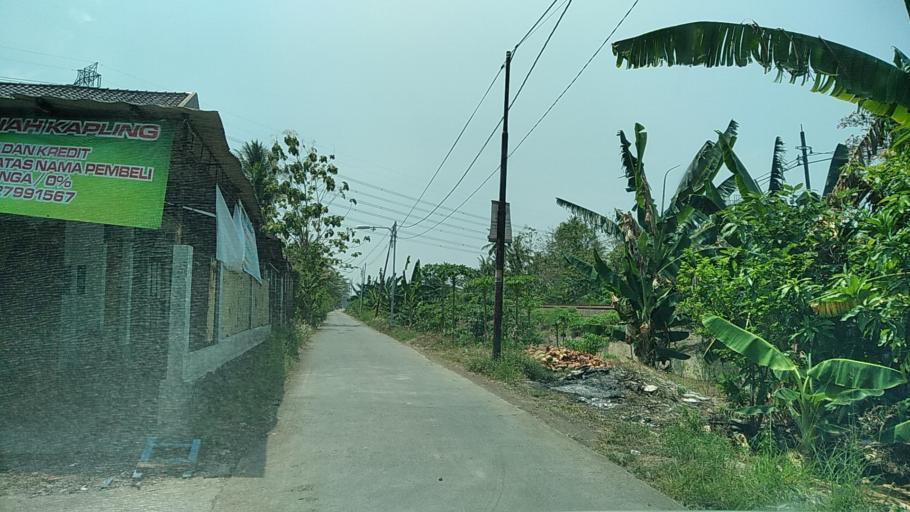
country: ID
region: Central Java
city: Mranggen
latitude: -6.9943
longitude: 110.4870
